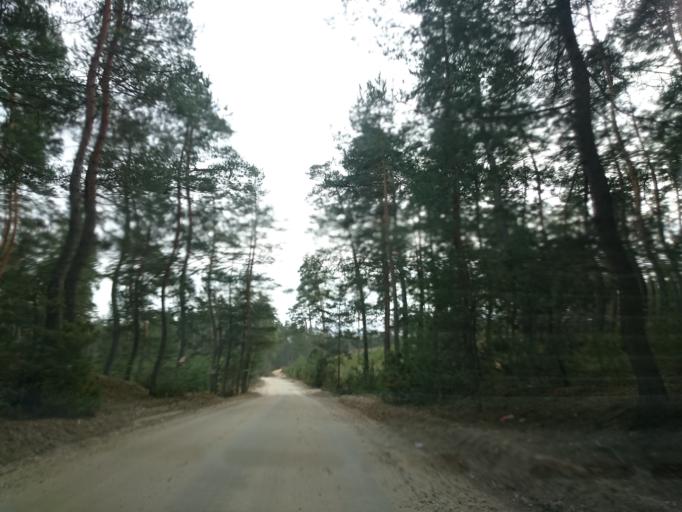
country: LV
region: Garkalne
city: Garkalne
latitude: 57.0303
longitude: 24.3819
